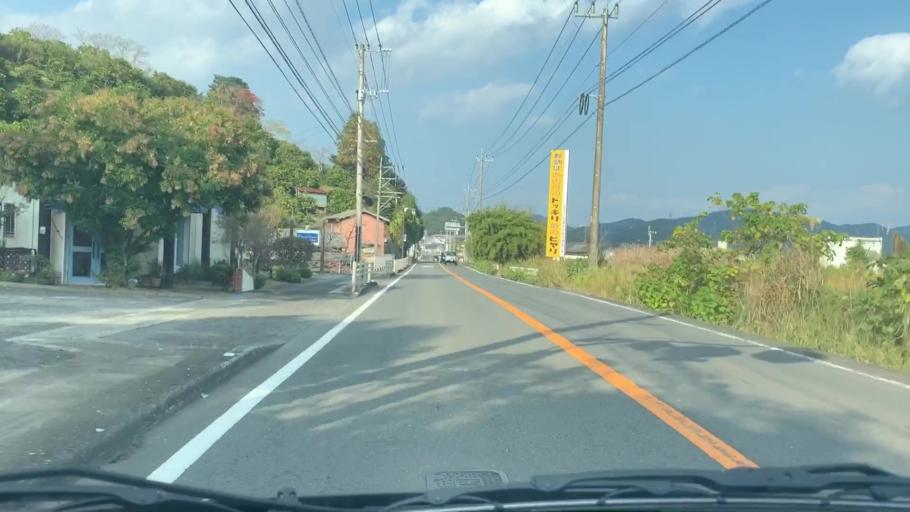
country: JP
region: Nagasaki
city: Togitsu
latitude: 32.9416
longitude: 129.7820
